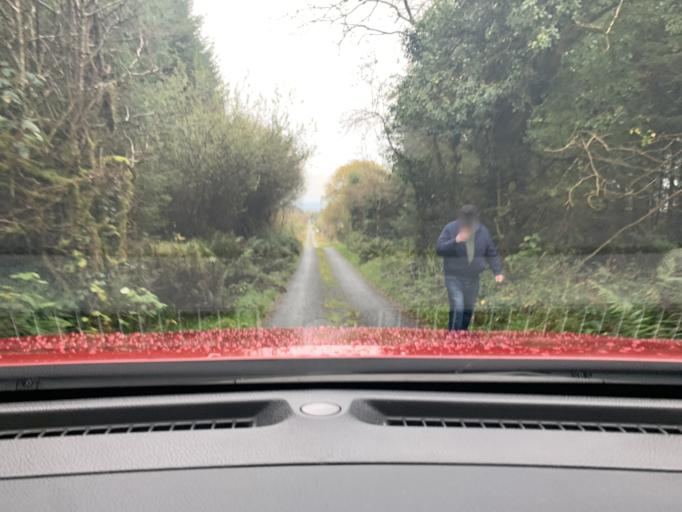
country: IE
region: Connaught
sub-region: Roscommon
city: Ballaghaderreen
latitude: 53.9238
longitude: -8.5629
